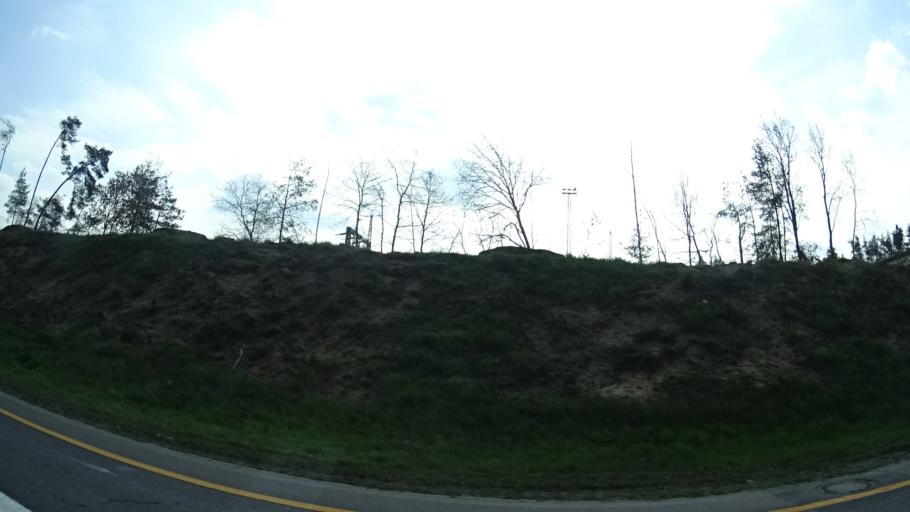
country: DE
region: Bavaria
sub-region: Regierungsbezirk Mittelfranken
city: Schwabach
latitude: 49.3254
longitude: 11.0507
